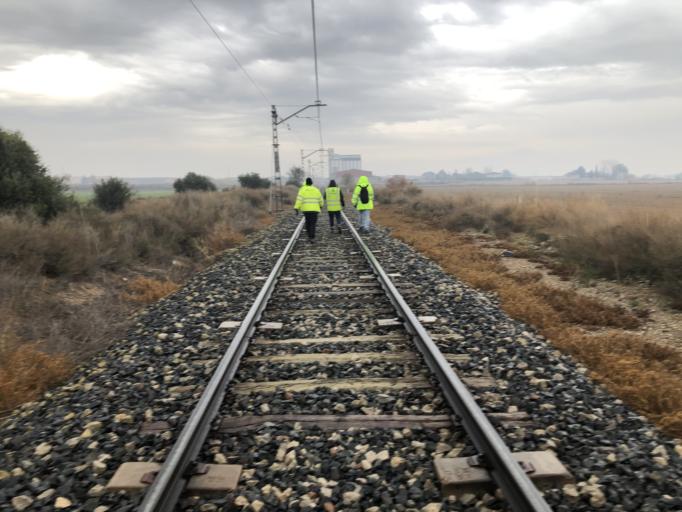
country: ES
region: Catalonia
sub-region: Provincia de Lleida
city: Bellvis
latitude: 41.6309
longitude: 0.7646
